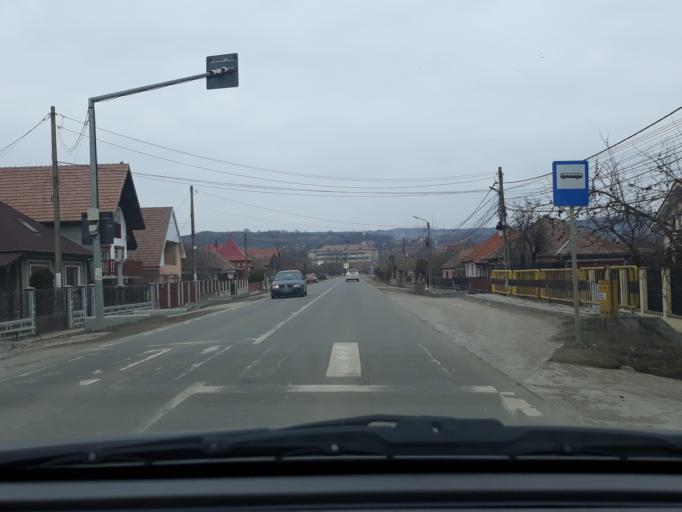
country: RO
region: Salaj
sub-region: Comuna Criseni
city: Criseni
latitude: 47.2245
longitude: 23.0396
